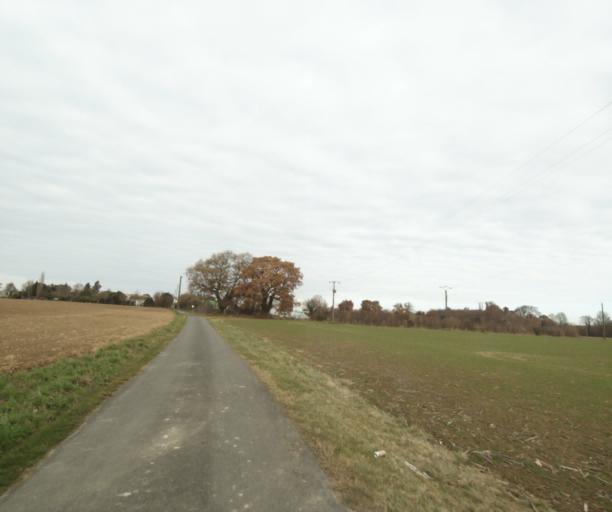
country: FR
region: Poitou-Charentes
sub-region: Departement de la Charente-Maritime
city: Corme-Royal
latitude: 45.7322
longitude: -0.7867
